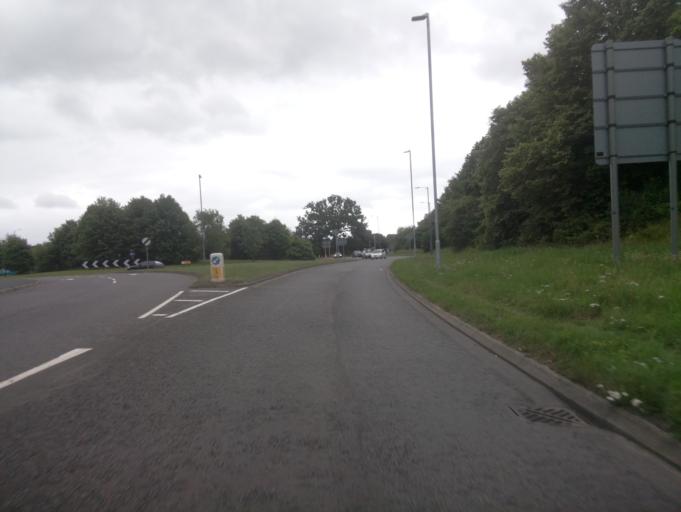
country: GB
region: England
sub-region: Worcestershire
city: Droitwich
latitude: 52.2528
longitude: -2.1634
